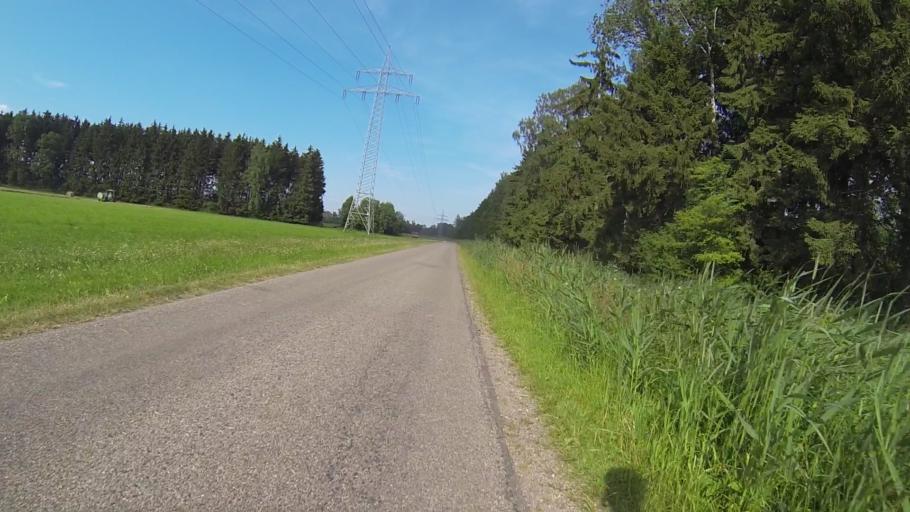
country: DE
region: Bavaria
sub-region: Swabia
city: Holzheim
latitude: 48.3784
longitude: 10.0594
